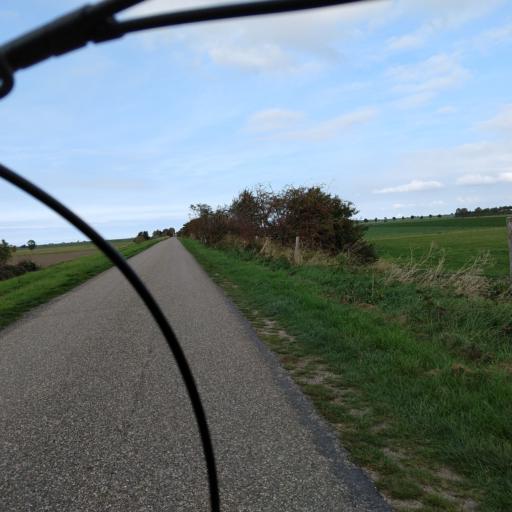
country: NL
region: South Holland
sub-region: Gemeente Goeree-Overflakkee
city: Ouddorp
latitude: 51.7179
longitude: 3.9475
